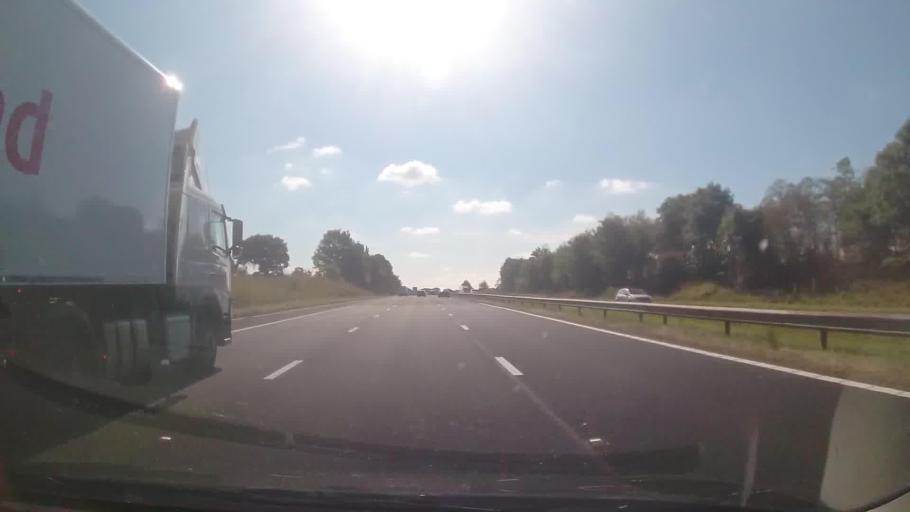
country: GB
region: England
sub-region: Lancashire
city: Goosnargh
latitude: 53.8299
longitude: -2.7189
